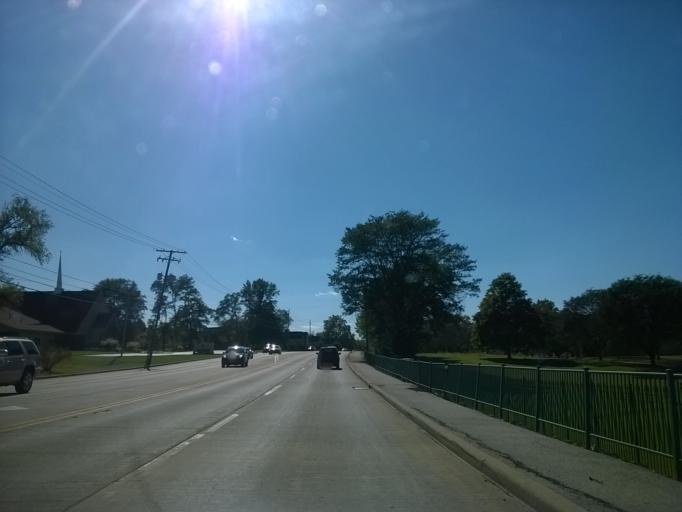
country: US
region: Indiana
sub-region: Hamilton County
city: Fishers
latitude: 39.9312
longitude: -86.0606
